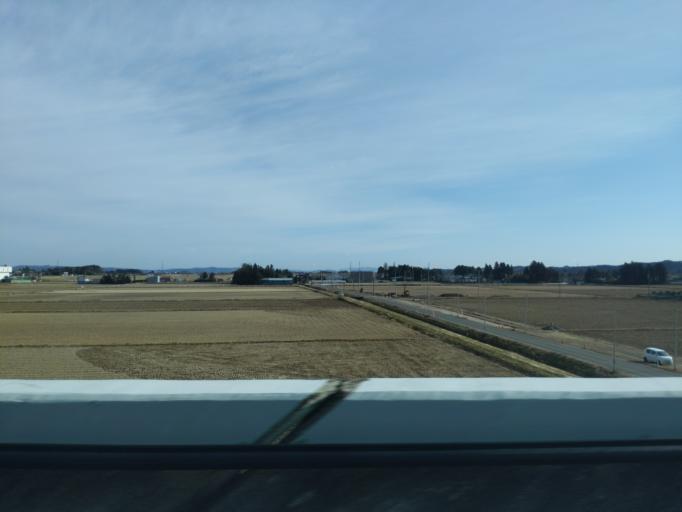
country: JP
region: Miyagi
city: Furukawa
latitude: 38.5357
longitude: 140.9609
